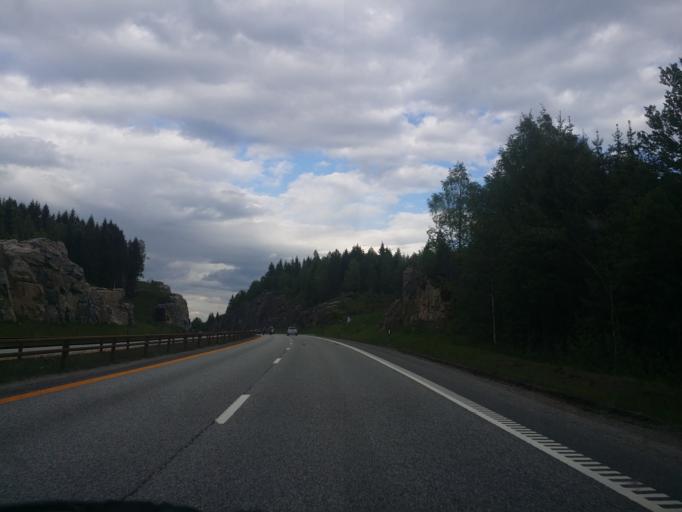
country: NO
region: Akershus
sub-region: Eidsvoll
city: Raholt
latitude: 60.3201
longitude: 11.1622
